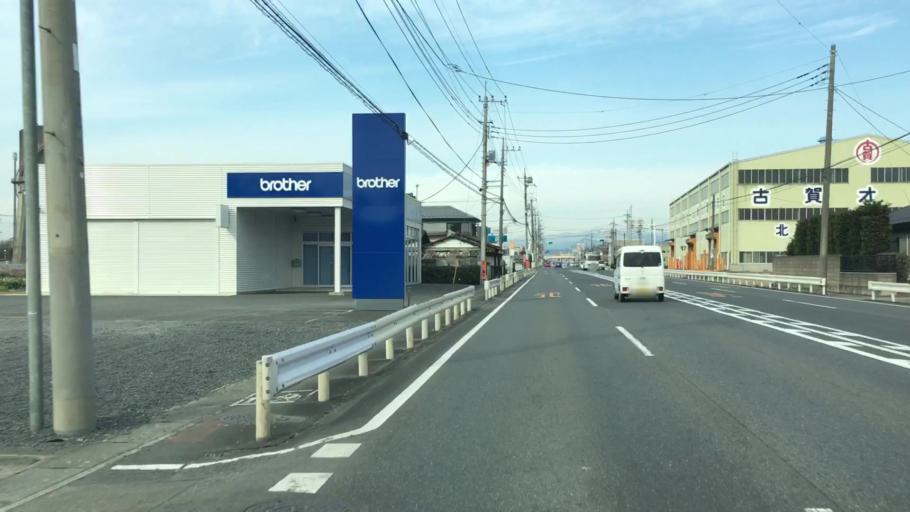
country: JP
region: Saitama
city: Menuma
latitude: 36.2505
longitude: 139.3788
